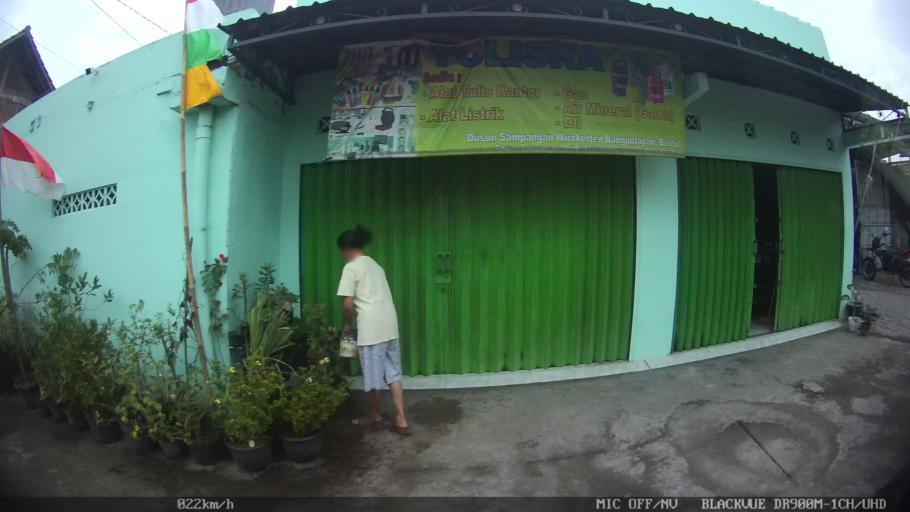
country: ID
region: Daerah Istimewa Yogyakarta
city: Sewon
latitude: -7.8544
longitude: 110.3965
